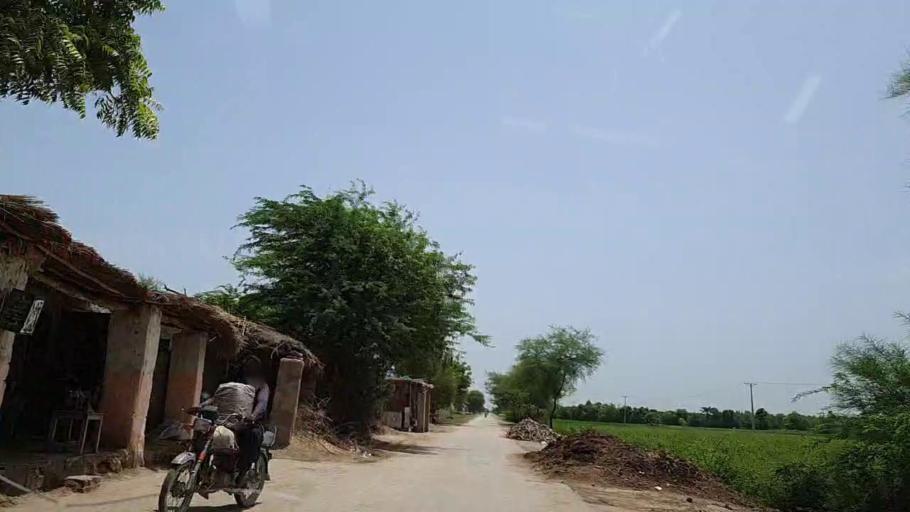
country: PK
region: Sindh
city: Tharu Shah
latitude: 26.9583
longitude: 68.0701
